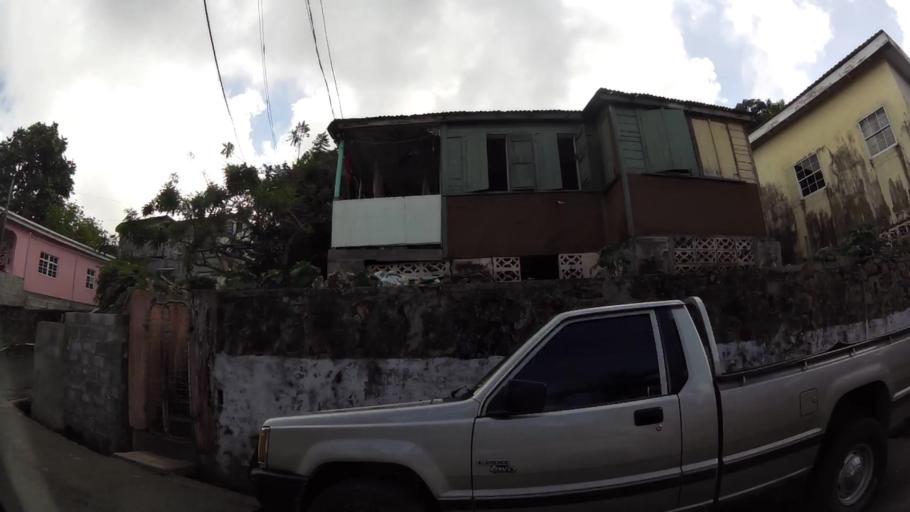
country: LC
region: Castries Quarter
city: Castries
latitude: 14.0041
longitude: -60.9861
